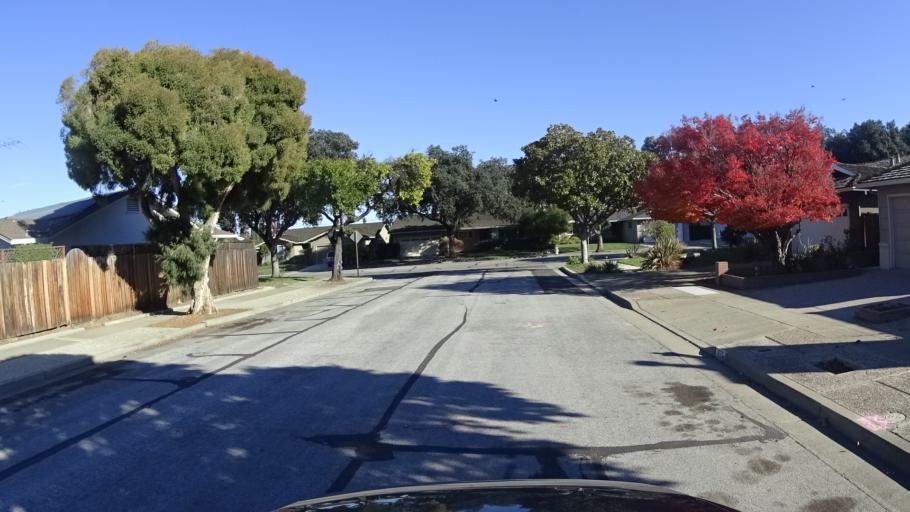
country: US
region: California
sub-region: Santa Clara County
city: Cupertino
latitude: 37.3465
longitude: -122.0244
